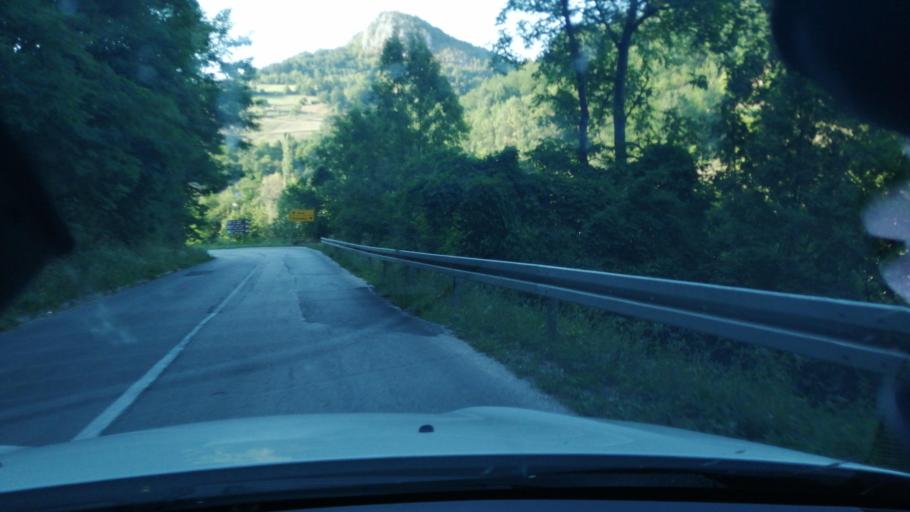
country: RS
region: Central Serbia
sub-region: Moravicki Okrug
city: Ivanjica
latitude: 43.6756
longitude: 20.2598
